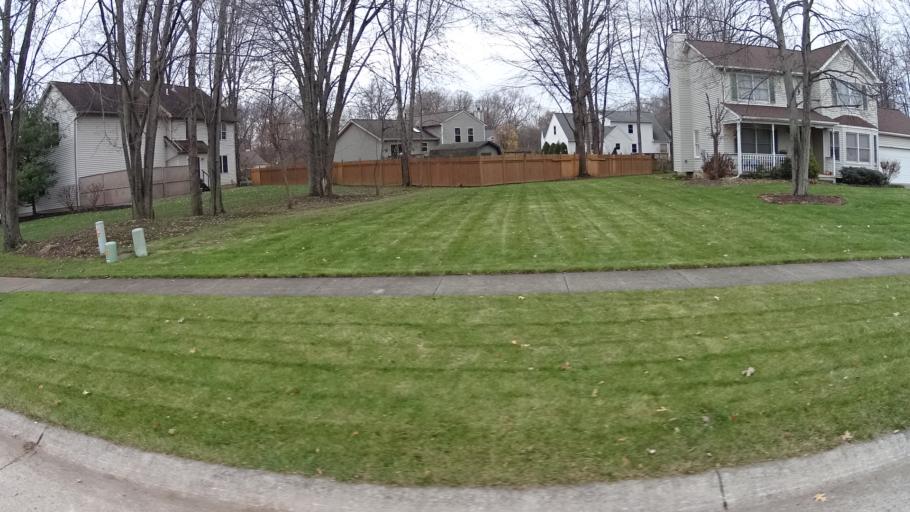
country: US
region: Ohio
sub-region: Lorain County
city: North Ridgeville
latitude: 41.3875
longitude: -82.0078
